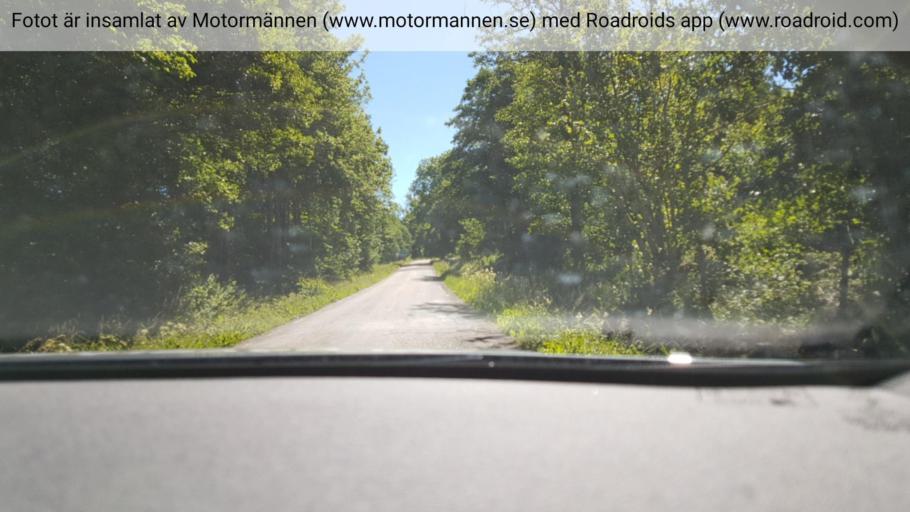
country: SE
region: Vaestra Goetaland
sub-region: Falkopings Kommun
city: Akarp
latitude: 58.1911
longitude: 13.7350
